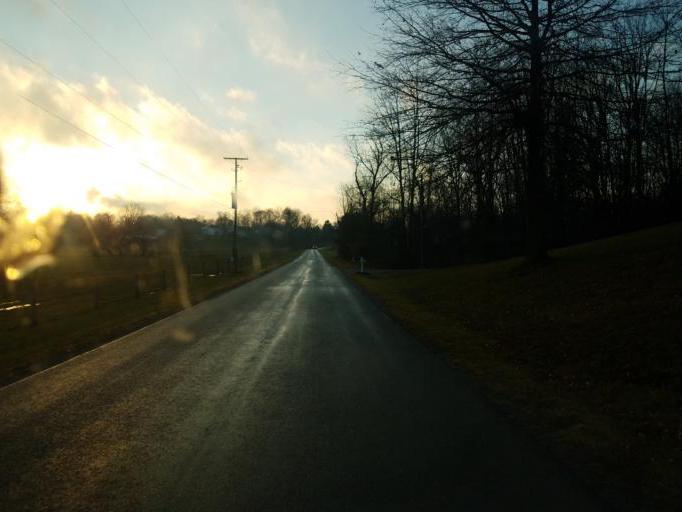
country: US
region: Ohio
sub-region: Knox County
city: Centerburg
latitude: 40.2395
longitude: -82.6805
